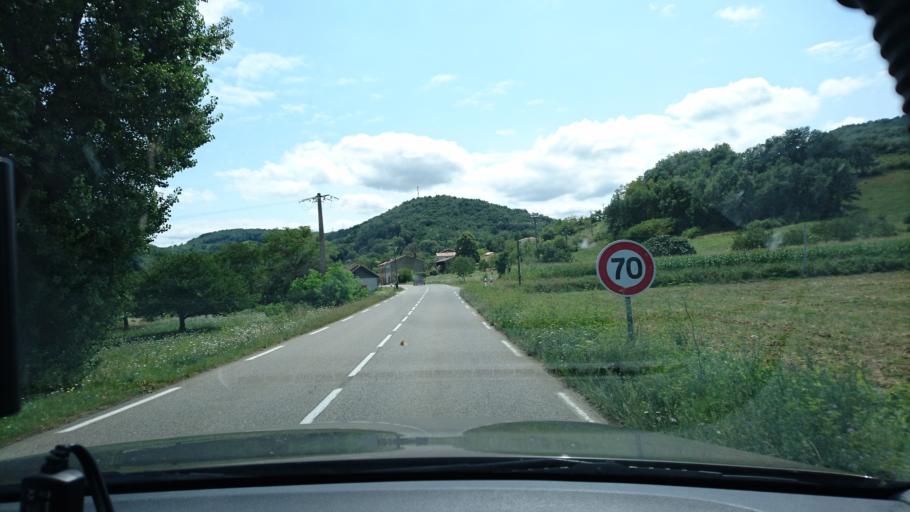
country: FR
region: Midi-Pyrenees
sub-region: Departement de la Haute-Garonne
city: Gaillac-Toulza
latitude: 43.1076
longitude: 1.4402
